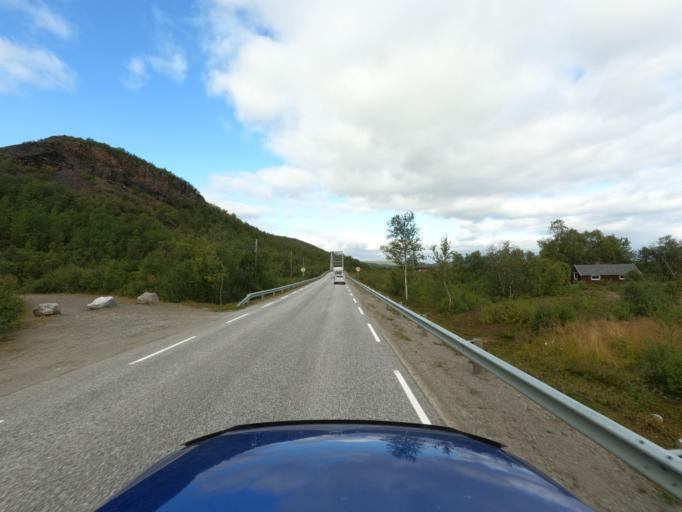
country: NO
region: Finnmark Fylke
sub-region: Porsanger
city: Lakselv
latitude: 70.1802
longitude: 24.9084
